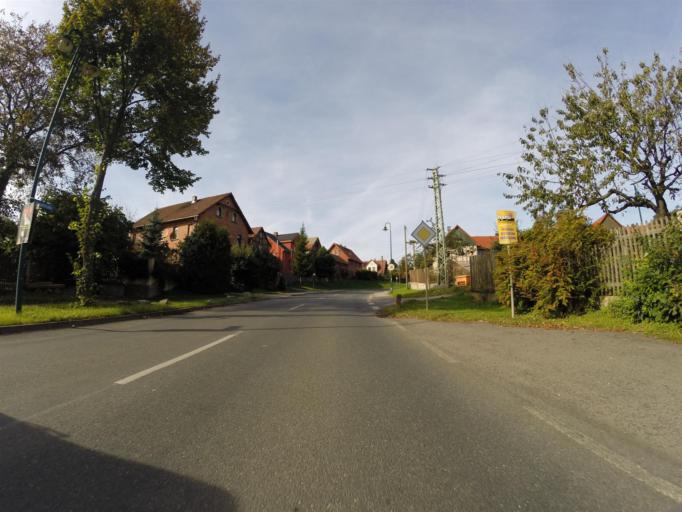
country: DE
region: Thuringia
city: Grossschwabhausen
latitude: 50.9593
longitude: 11.5176
